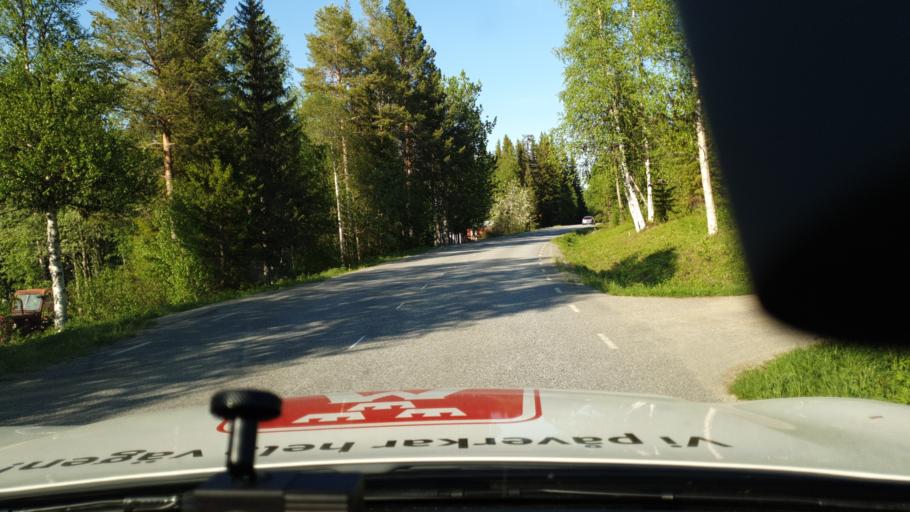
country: SE
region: Vaesterbotten
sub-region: Storumans Kommun
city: Storuman
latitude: 64.7019
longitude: 17.1212
